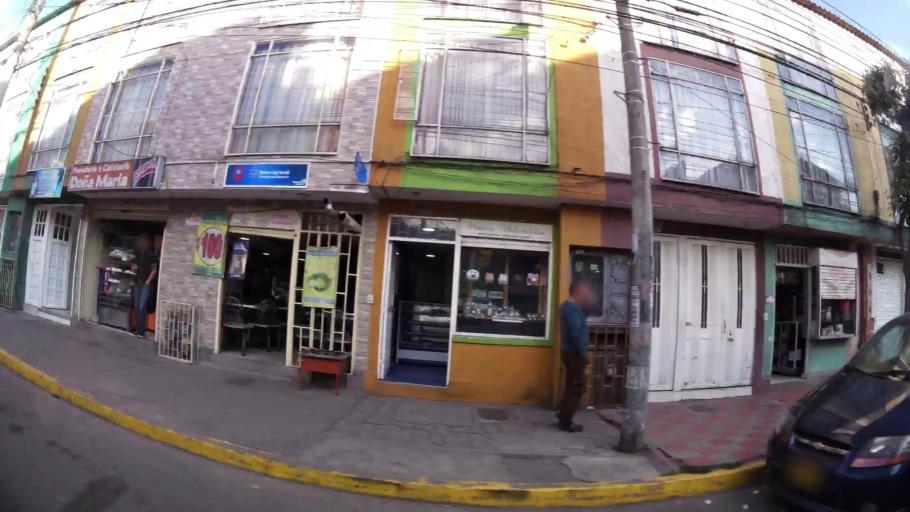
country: CO
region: Cundinamarca
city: Soacha
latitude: 4.5709
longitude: -74.1444
